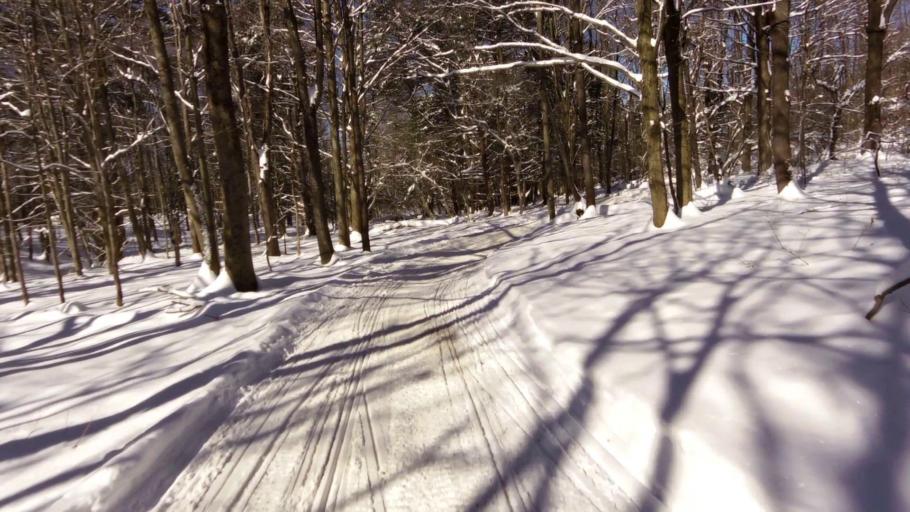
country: US
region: New York
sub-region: Chautauqua County
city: Mayville
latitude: 42.2379
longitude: -79.4221
